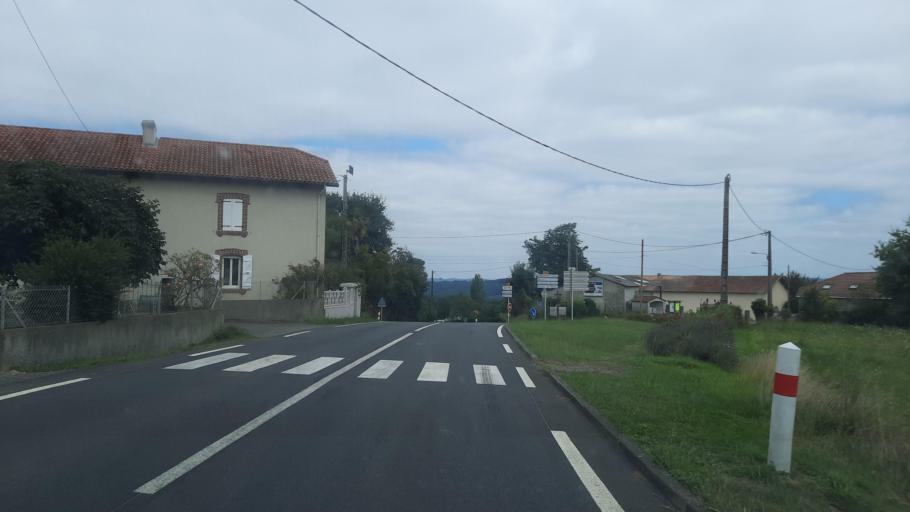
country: FR
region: Midi-Pyrenees
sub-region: Departement des Hautes-Pyrenees
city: Orleix
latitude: 43.2672
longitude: 0.1577
